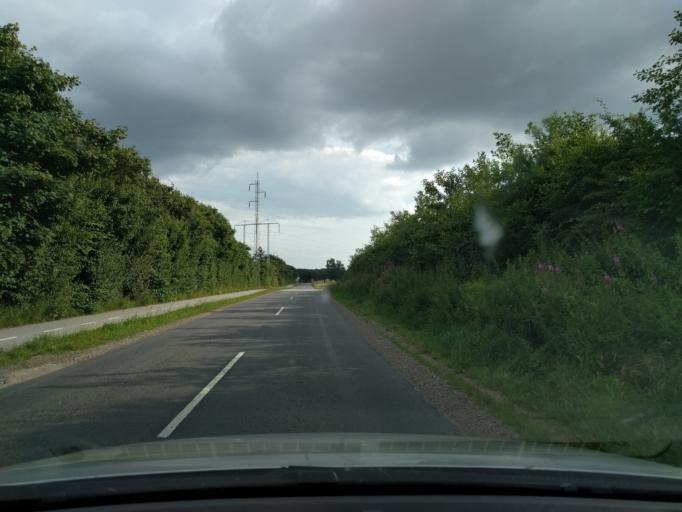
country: DK
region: Central Jutland
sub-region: Herning Kommune
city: Snejbjerg
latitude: 56.1104
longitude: 8.9080
